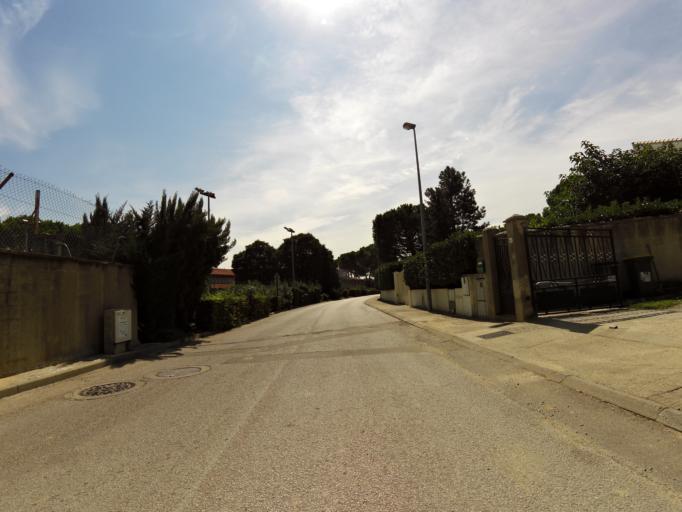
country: FR
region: Languedoc-Roussillon
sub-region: Departement du Gard
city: Vergeze
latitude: 43.7485
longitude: 4.2222
